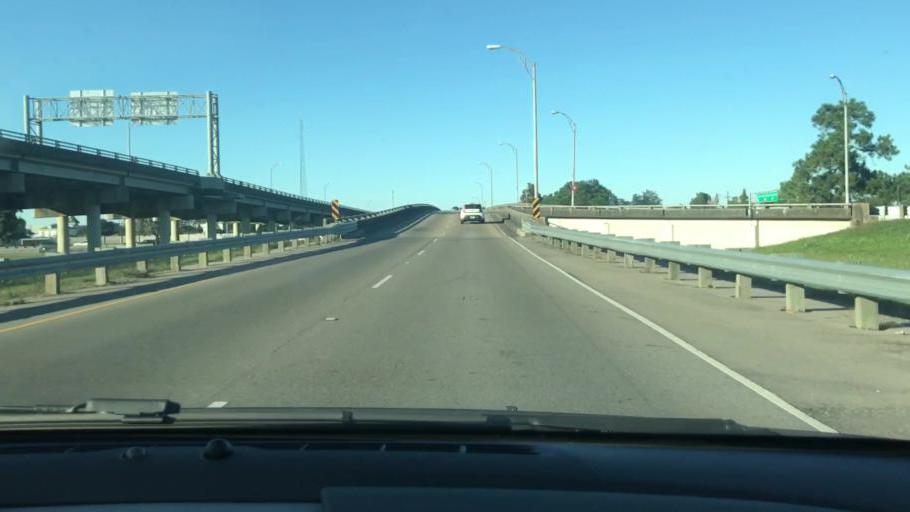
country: US
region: Louisiana
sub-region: Jefferson Parish
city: Metairie
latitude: 29.9935
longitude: -90.1158
